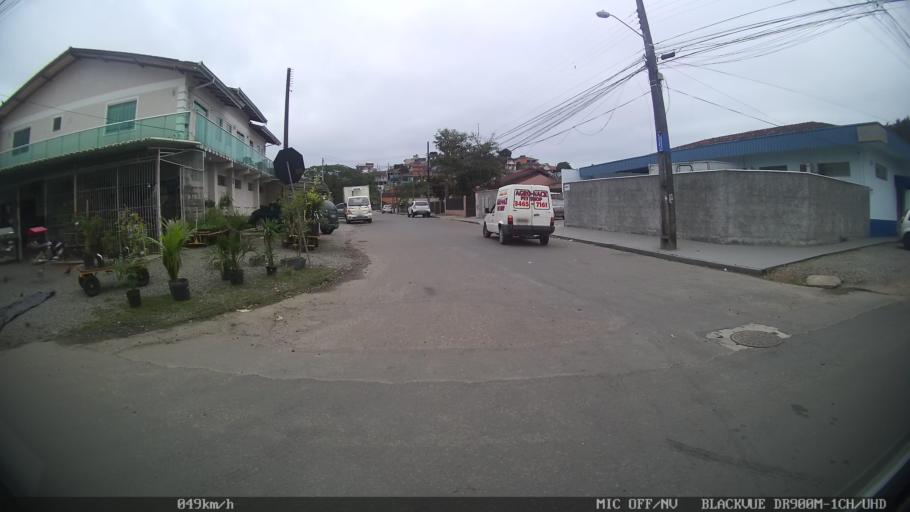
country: BR
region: Santa Catarina
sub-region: Joinville
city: Joinville
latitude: -26.3323
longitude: -48.8132
